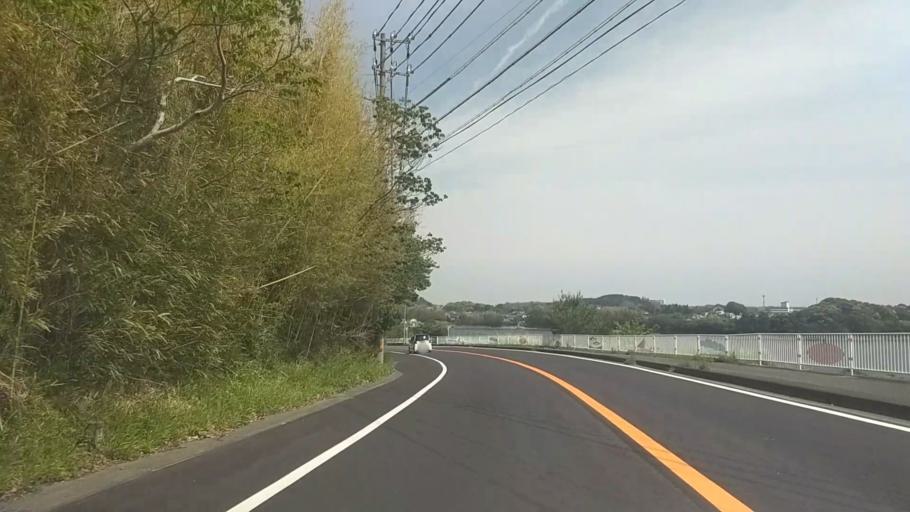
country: JP
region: Shizuoka
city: Kosai-shi
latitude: 34.7967
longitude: 137.5646
